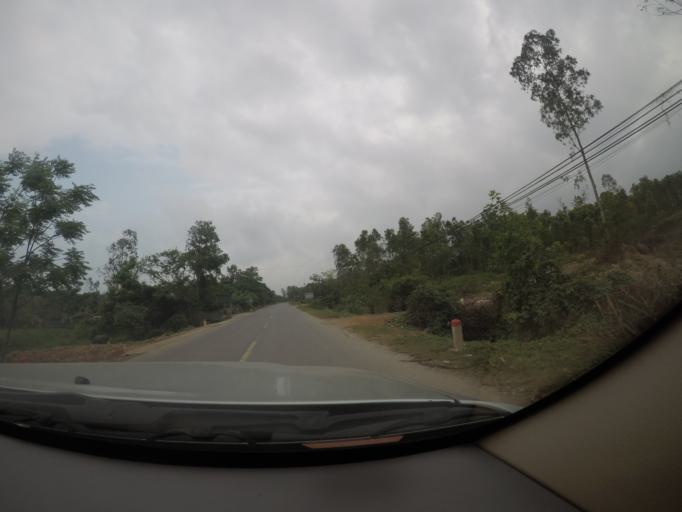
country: VN
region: Quang Binh
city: Kien Giang
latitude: 17.2216
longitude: 106.7077
